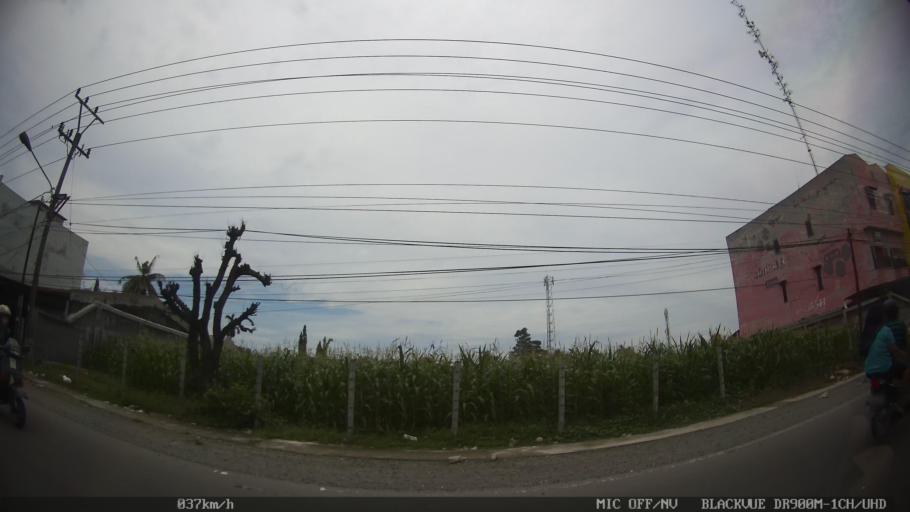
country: ID
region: North Sumatra
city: Sunggal
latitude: 3.5995
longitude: 98.5560
